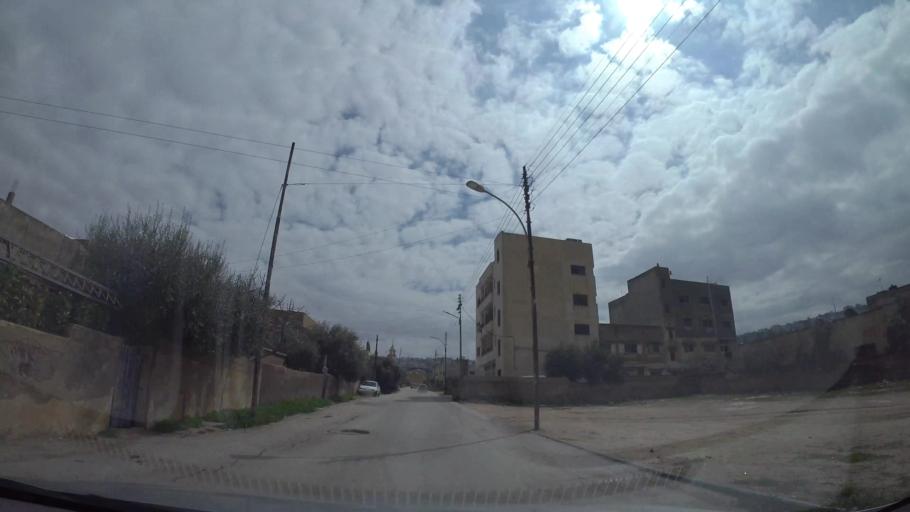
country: JO
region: Amman
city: Al Jubayhah
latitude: 32.0538
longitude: 35.8261
